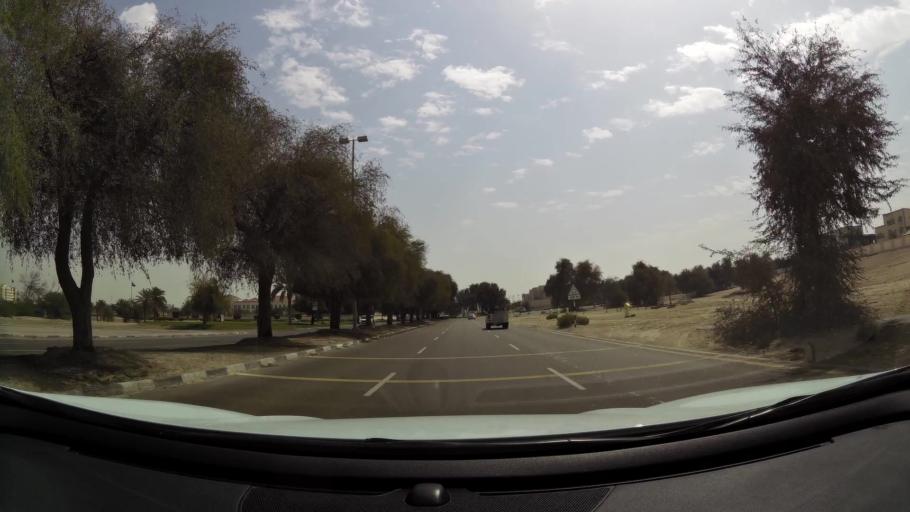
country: AE
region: Abu Dhabi
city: Abu Dhabi
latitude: 24.3083
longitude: 54.6169
